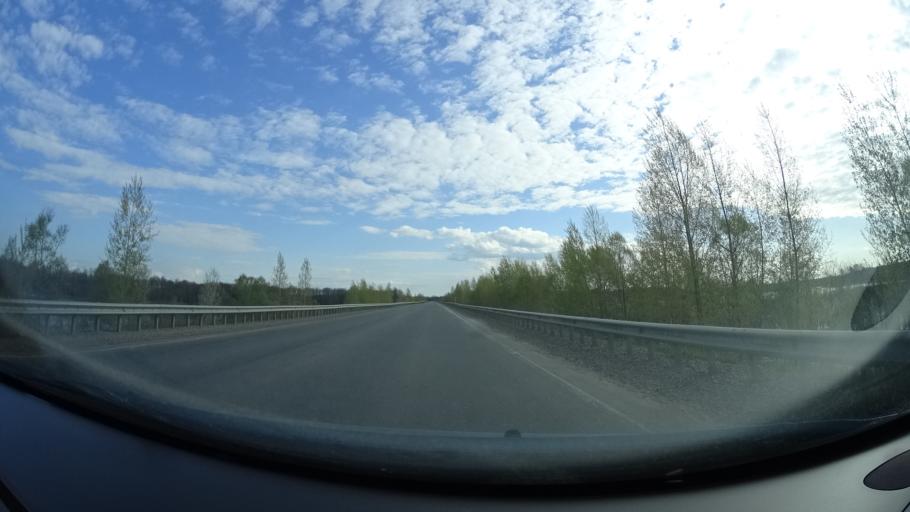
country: RU
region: Bashkortostan
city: Blagoveshchensk
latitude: 55.0219
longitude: 55.7901
